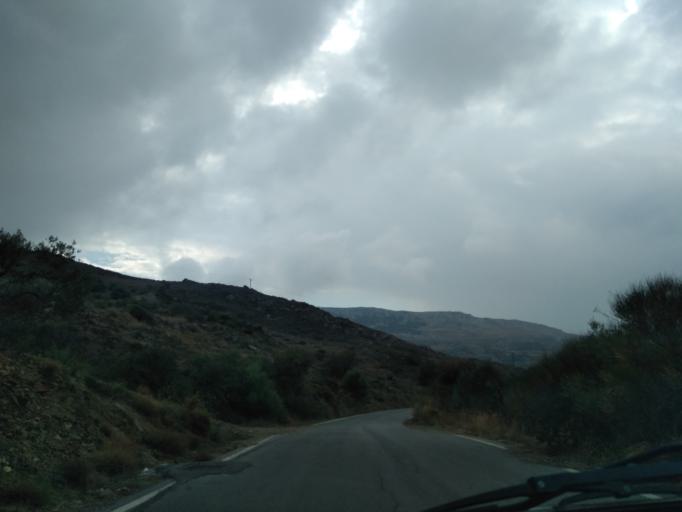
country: GR
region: Crete
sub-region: Nomos Lasithiou
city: Siteia
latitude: 35.1424
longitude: 26.0238
